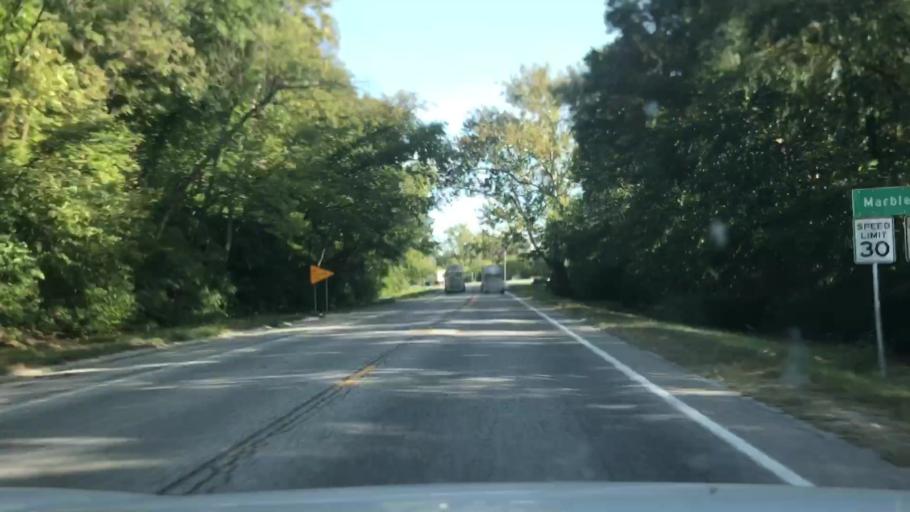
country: US
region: Illinois
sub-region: Adams County
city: Quincy
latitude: 39.8435
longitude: -91.3726
